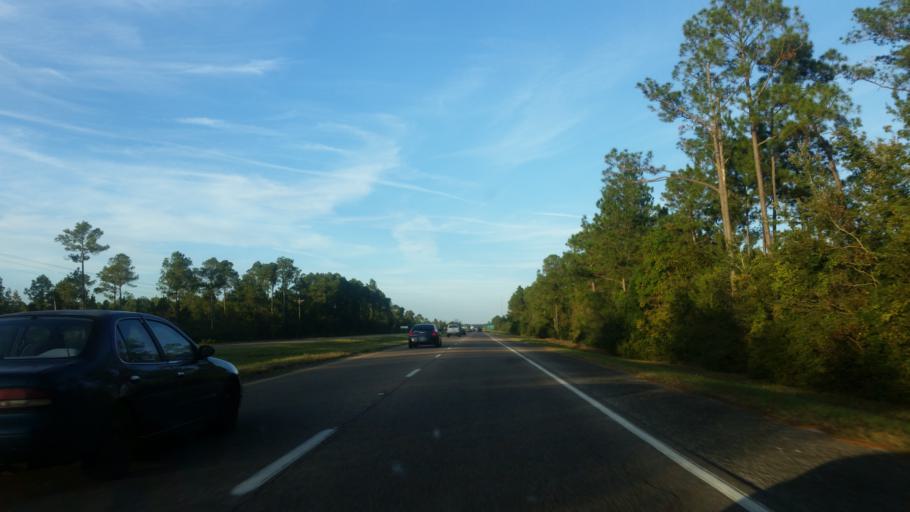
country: US
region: Mississippi
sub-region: Jackson County
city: Helena
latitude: 30.4491
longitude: -88.4255
